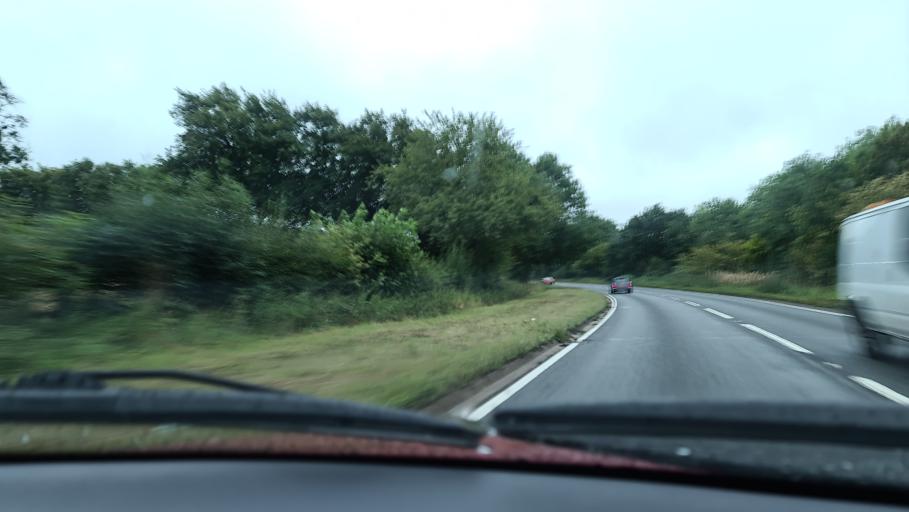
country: GB
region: England
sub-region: Buckinghamshire
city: Amersham
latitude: 51.6448
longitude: -0.6194
